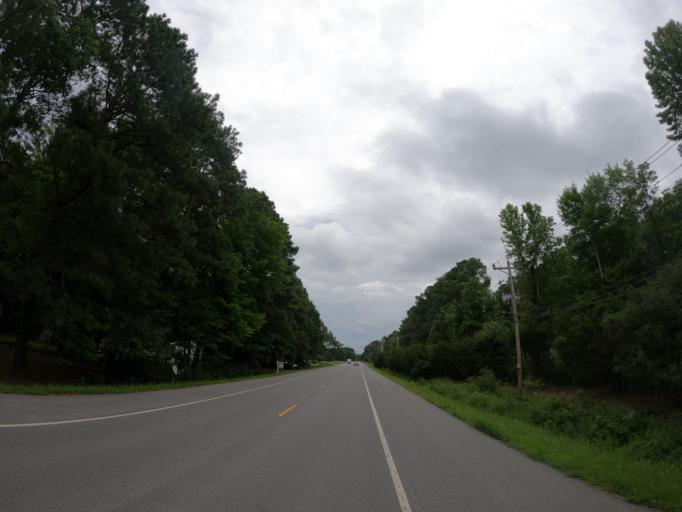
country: US
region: Maryland
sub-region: Saint Mary's County
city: Lexington Park
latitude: 38.1575
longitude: -76.5219
